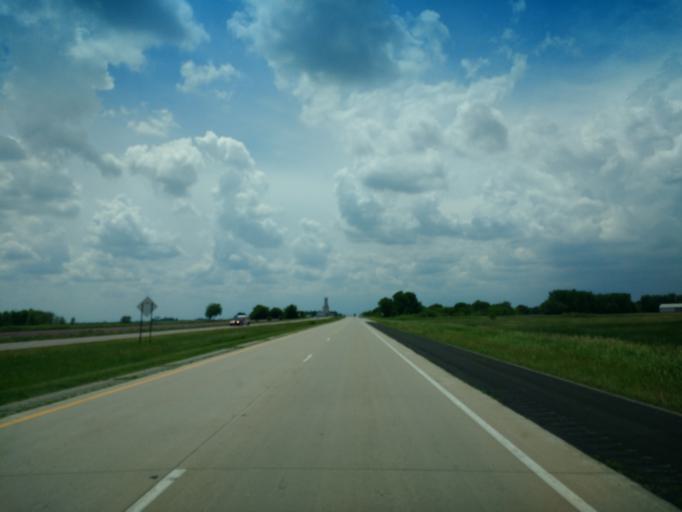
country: US
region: Minnesota
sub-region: Jackson County
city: Lakefield
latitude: 43.7793
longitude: -95.3476
